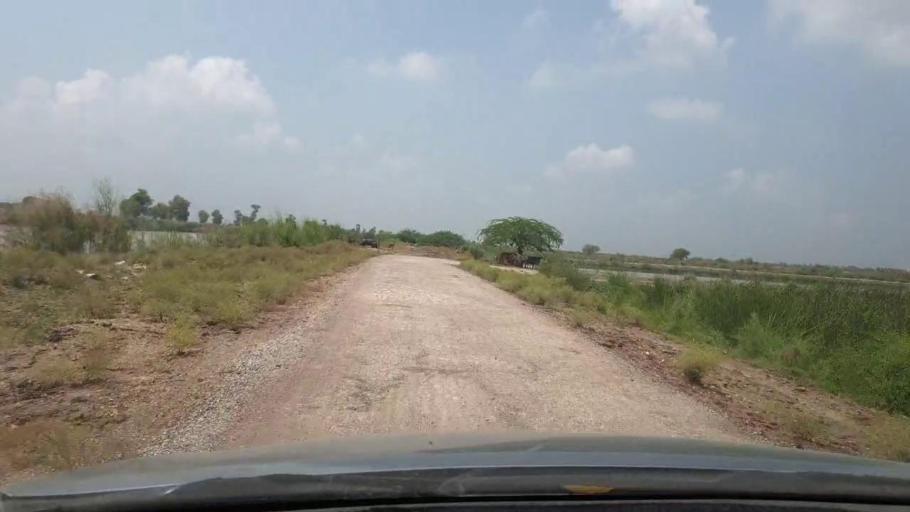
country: PK
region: Sindh
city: Khairpur
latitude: 27.4755
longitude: 68.7025
